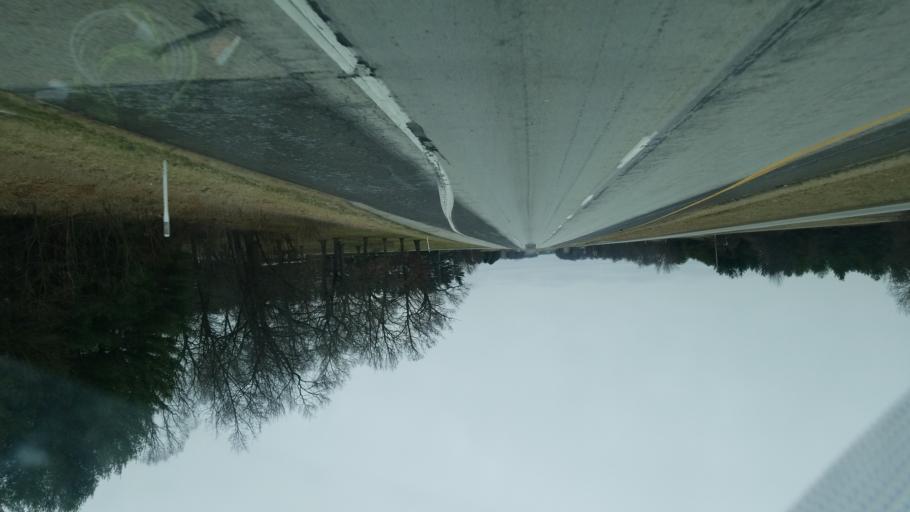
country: US
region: Indiana
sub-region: Fulton County
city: Rochester
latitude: 41.0702
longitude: -86.2401
